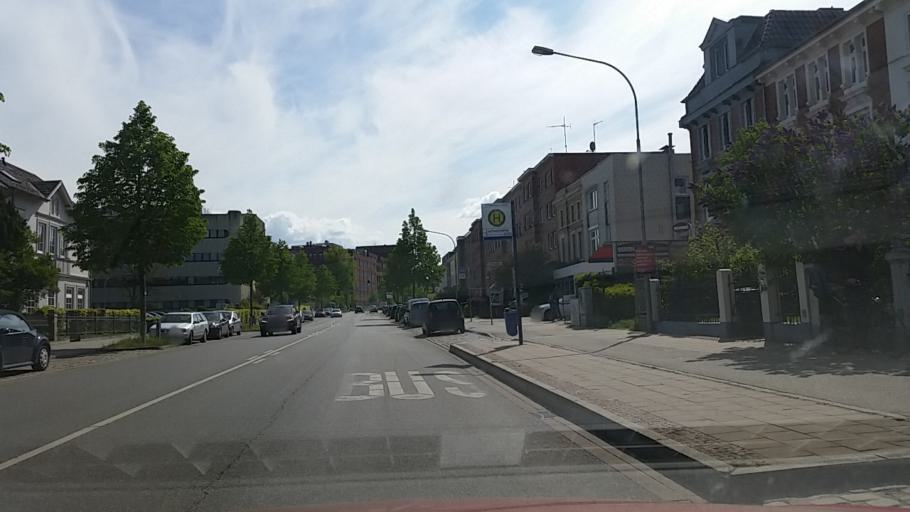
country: DE
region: Schleswig-Holstein
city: Luebeck
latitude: 53.8604
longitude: 10.6726
